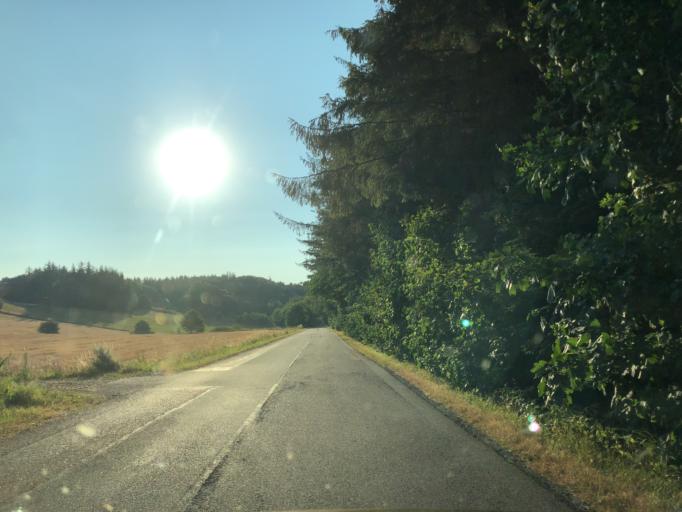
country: DK
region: Central Jutland
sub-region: Skanderborg Kommune
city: Stilling
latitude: 56.0984
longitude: 9.9520
